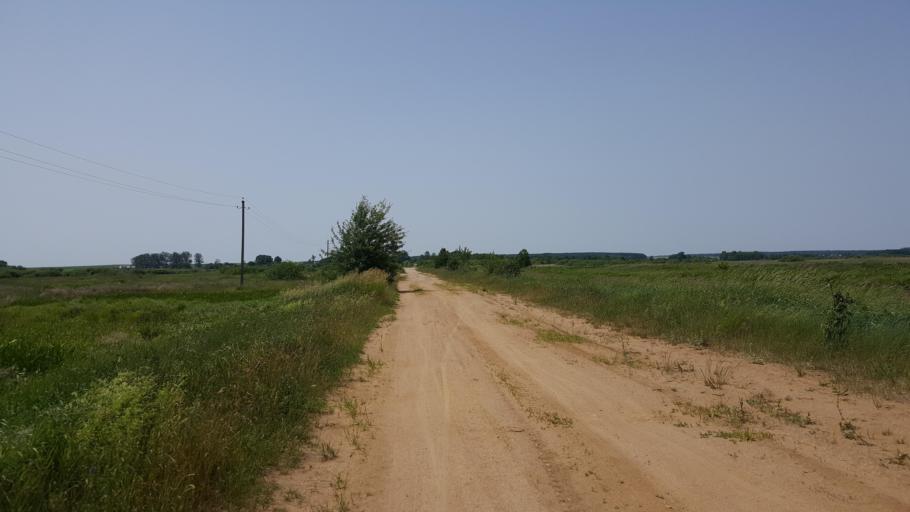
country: BY
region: Brest
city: Kamyanyets
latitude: 52.4756
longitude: 23.9032
